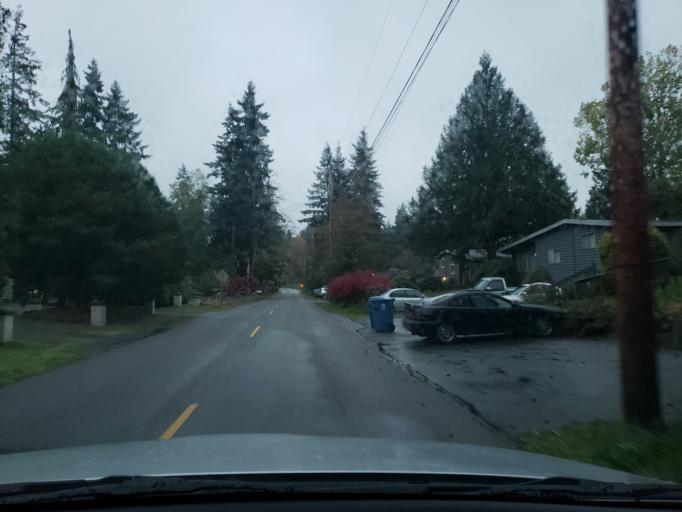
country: US
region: Washington
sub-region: Snohomish County
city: Meadowdale
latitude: 47.8335
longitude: -122.3306
